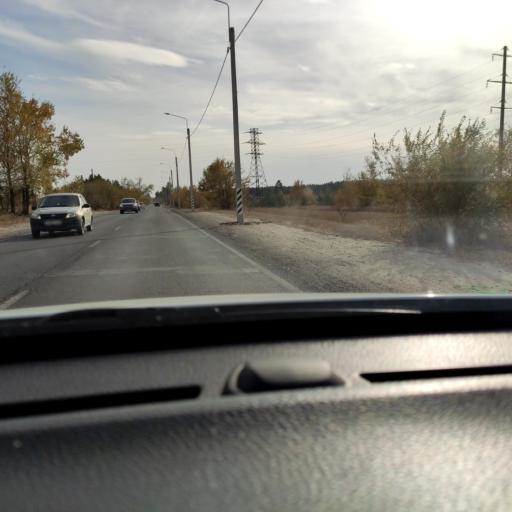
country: RU
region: Voronezj
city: Maslovka
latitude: 51.5791
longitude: 39.2472
